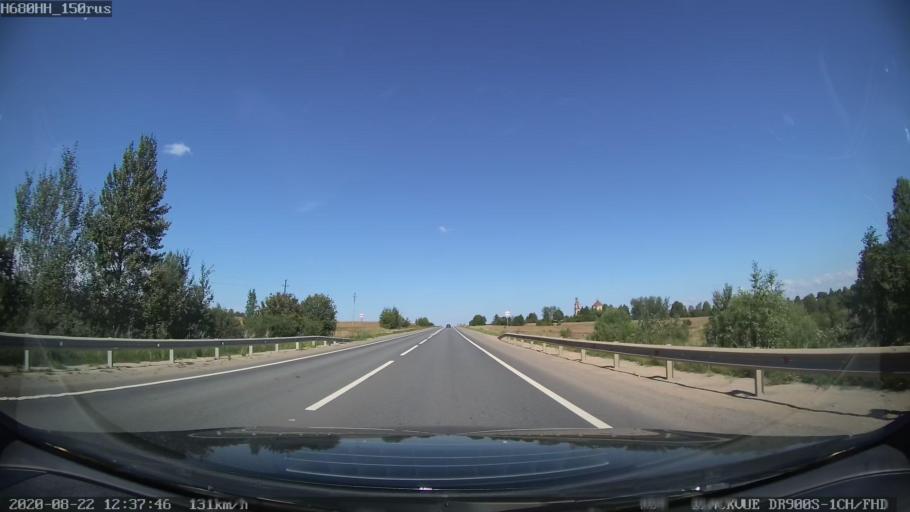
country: RU
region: Tverskaya
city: Rameshki
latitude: 57.3020
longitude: 36.0888
